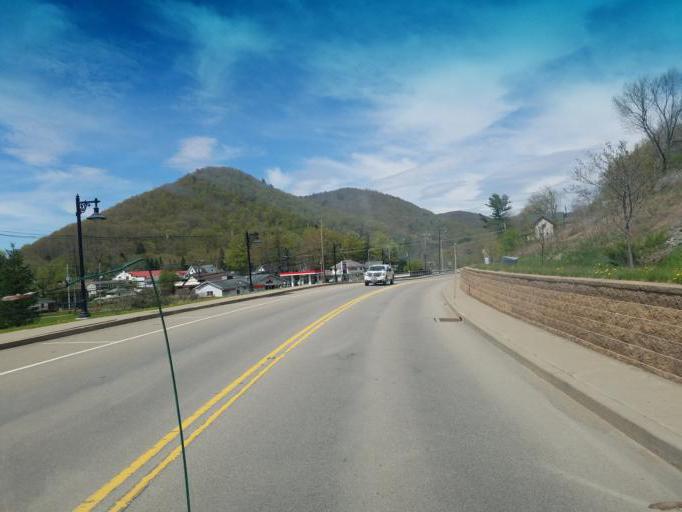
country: US
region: Pennsylvania
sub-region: Potter County
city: Galeton
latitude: 41.7354
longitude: -77.6458
